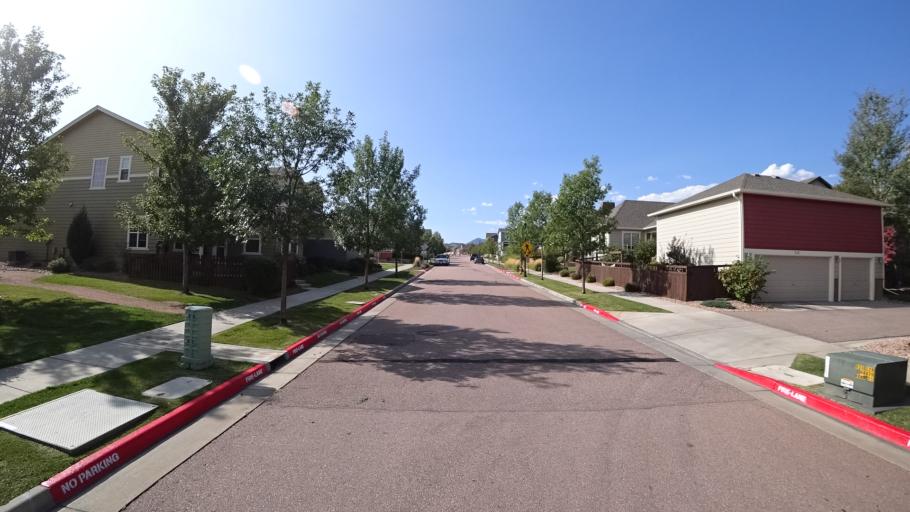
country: US
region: Colorado
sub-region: El Paso County
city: Colorado Springs
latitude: 38.8307
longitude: -104.8547
